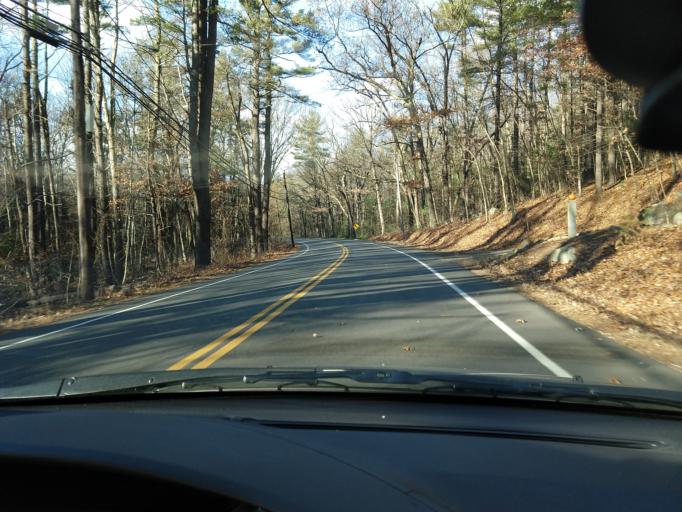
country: US
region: Massachusetts
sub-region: Middlesex County
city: Westford
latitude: 42.5444
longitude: -71.4080
